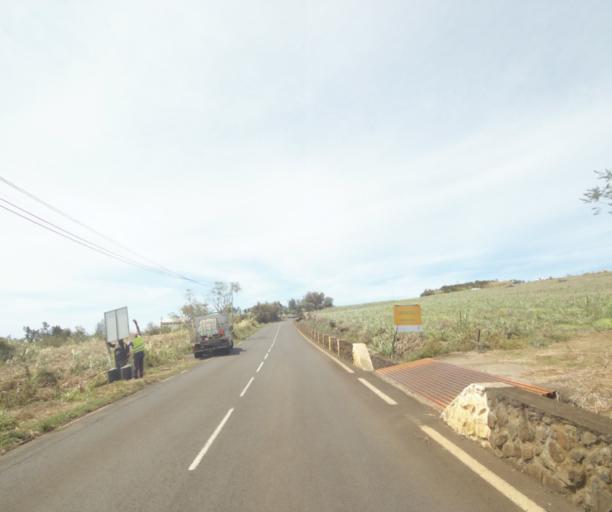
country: RE
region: Reunion
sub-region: Reunion
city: Saint-Paul
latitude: -21.0402
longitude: 55.2879
